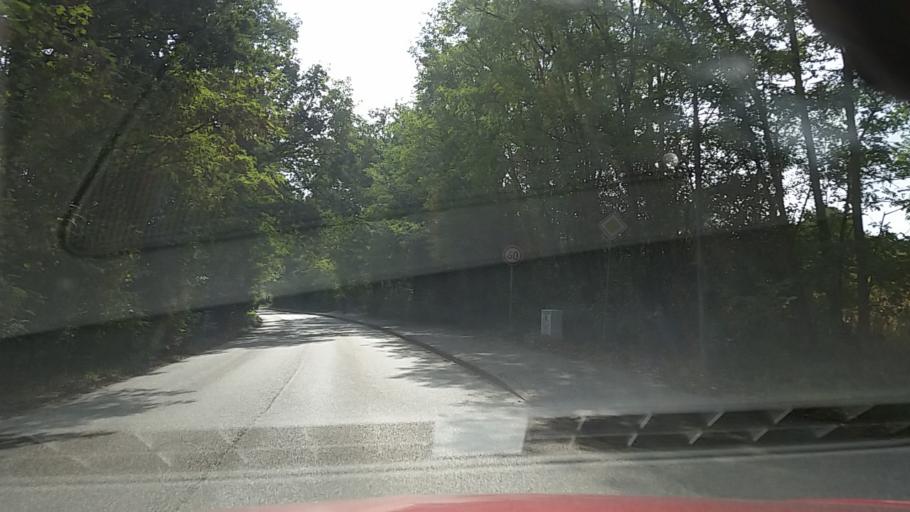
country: DE
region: Schleswig-Holstein
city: Appen
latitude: 53.6329
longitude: 9.7677
